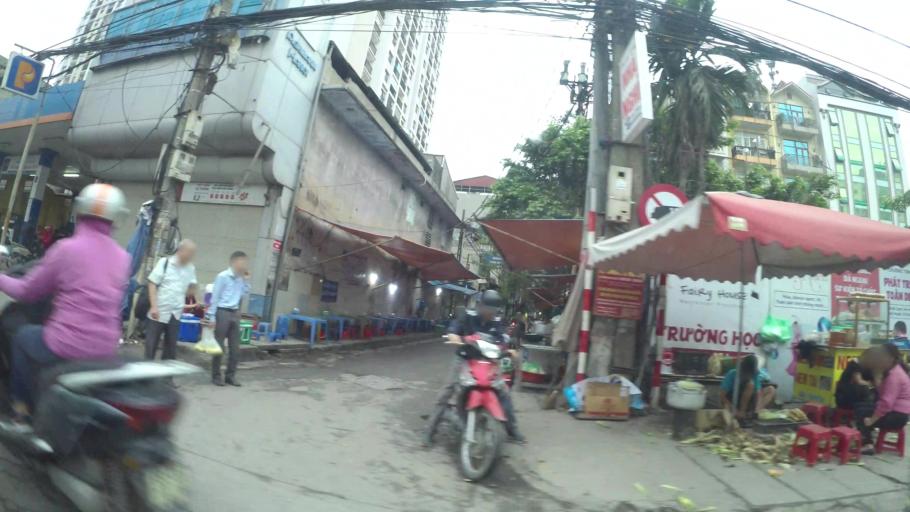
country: VN
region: Ha Noi
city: Hai BaTrung
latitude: 20.9943
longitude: 105.8628
